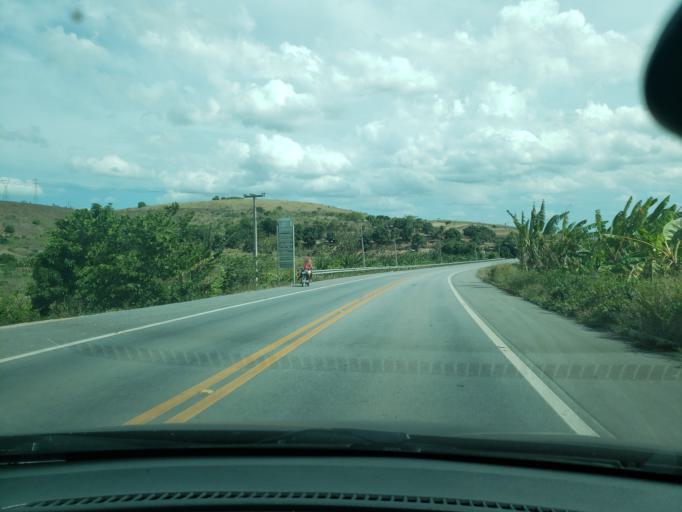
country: BR
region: Alagoas
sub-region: Murici
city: Murici
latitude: -9.2816
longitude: -35.9631
